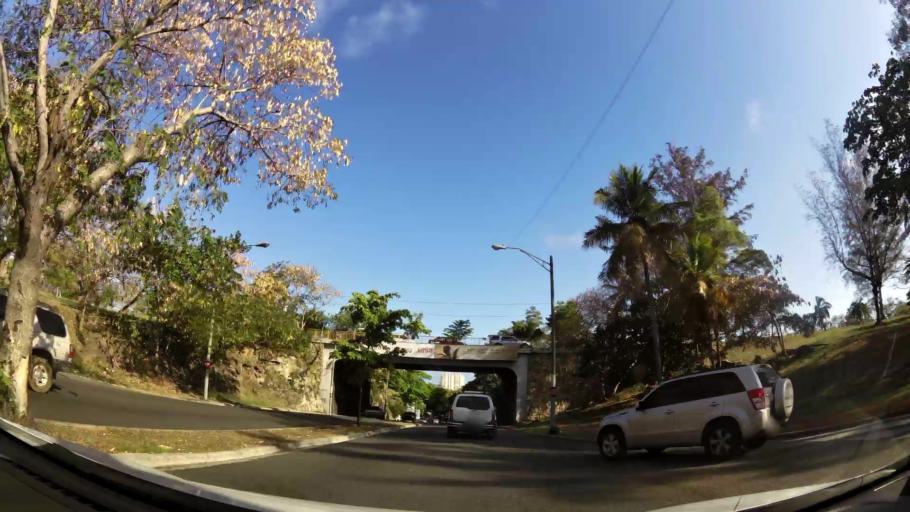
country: DO
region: Nacional
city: Bella Vista
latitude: 18.4511
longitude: -69.9371
